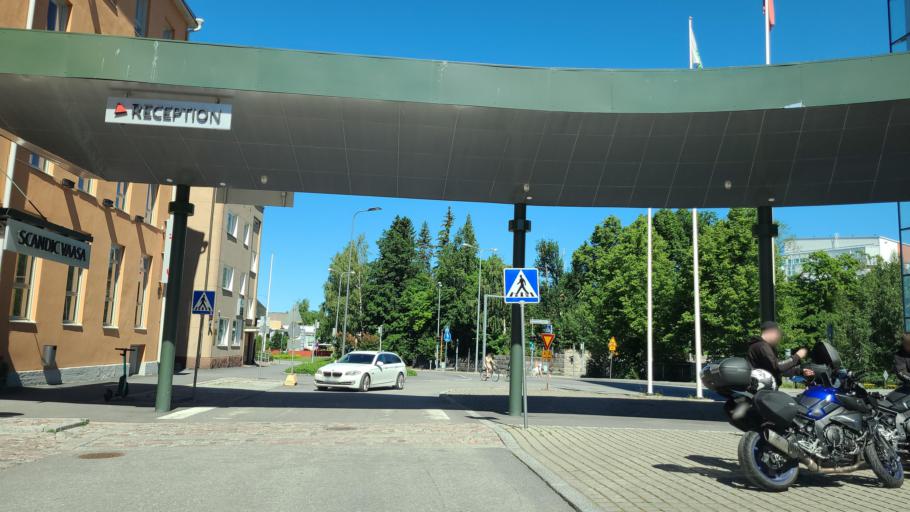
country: FI
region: Ostrobothnia
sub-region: Vaasa
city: Vaasa
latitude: 63.0980
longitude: 21.6191
